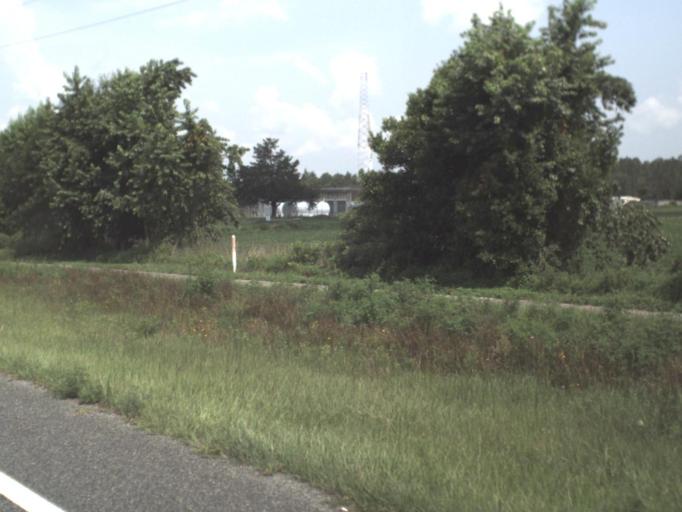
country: US
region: Florida
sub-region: Levy County
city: Chiefland
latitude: 29.4751
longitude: -82.8422
